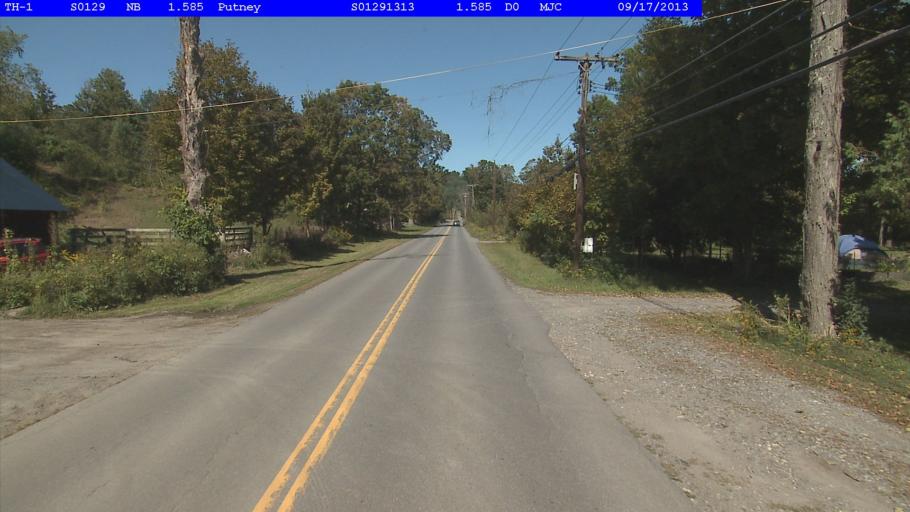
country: US
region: New Hampshire
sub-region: Cheshire County
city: Westmoreland
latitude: 42.9954
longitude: -72.5321
